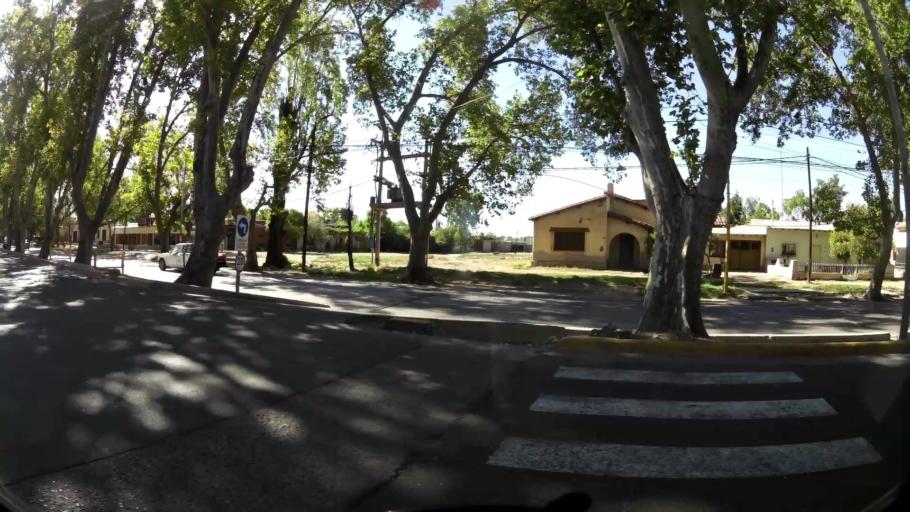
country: AR
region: Mendoza
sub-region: Departamento de Godoy Cruz
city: Godoy Cruz
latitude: -32.9445
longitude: -68.8138
